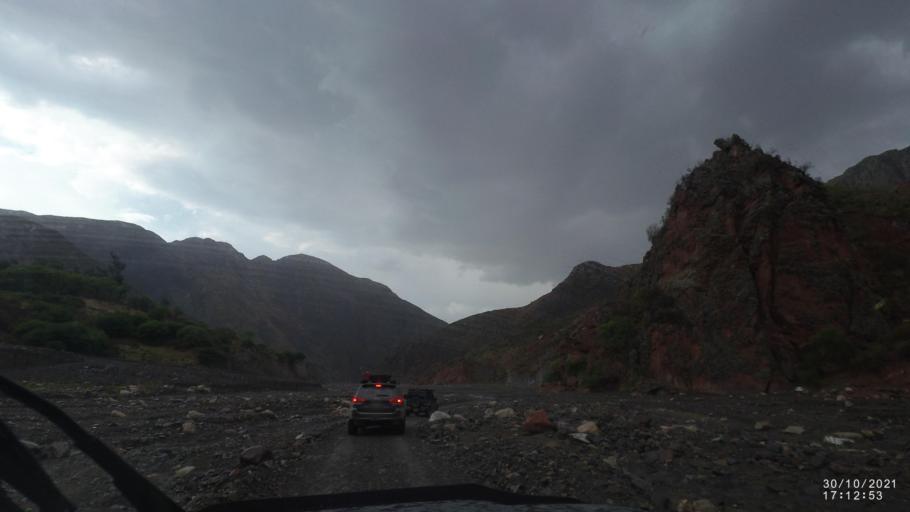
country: BO
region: Cochabamba
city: Colchani
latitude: -17.5503
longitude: -66.6257
